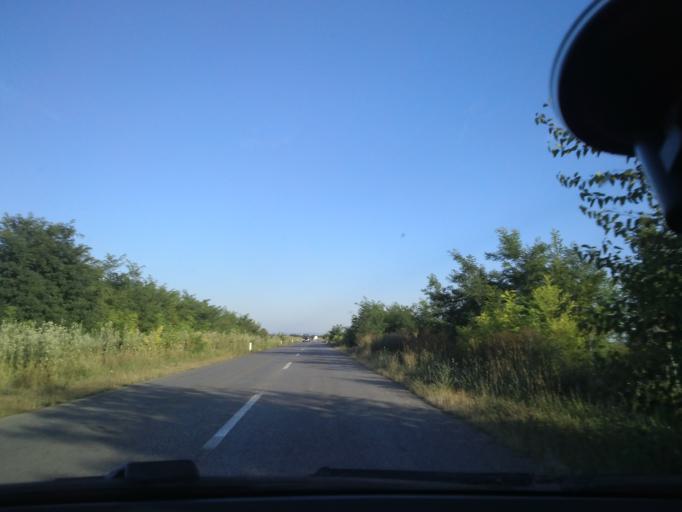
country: RS
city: Obrovac
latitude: 45.4328
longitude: 19.3797
